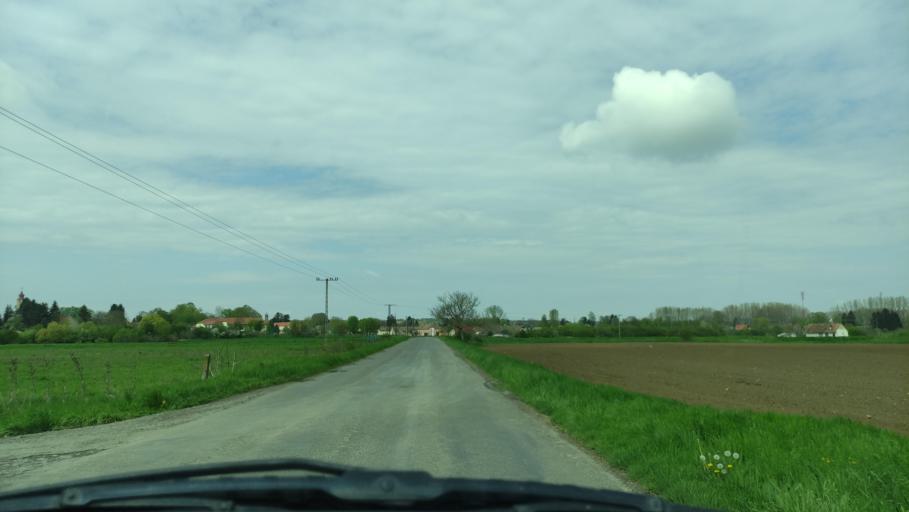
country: HU
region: Baranya
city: Sasd
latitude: 46.3062
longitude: 18.1427
